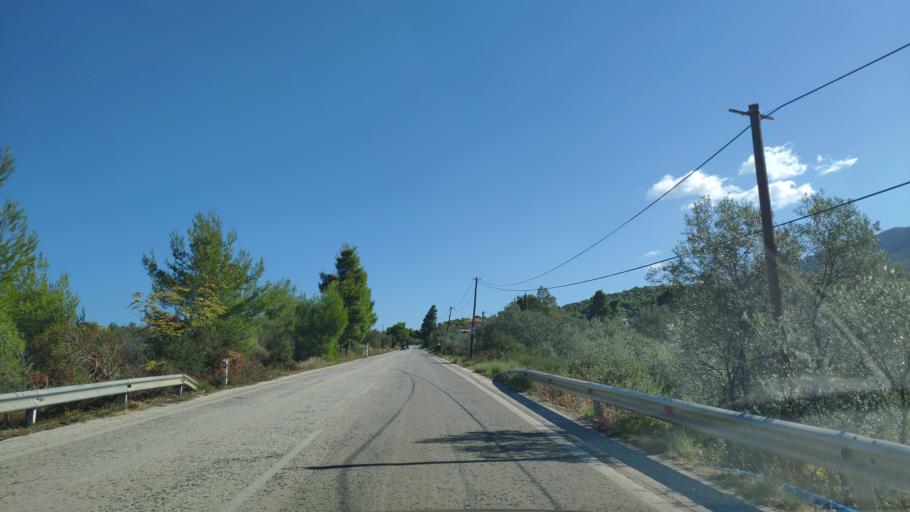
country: GR
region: Peloponnese
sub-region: Nomos Korinthias
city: Loutra Oraias Elenis
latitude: 37.8367
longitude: 23.0083
